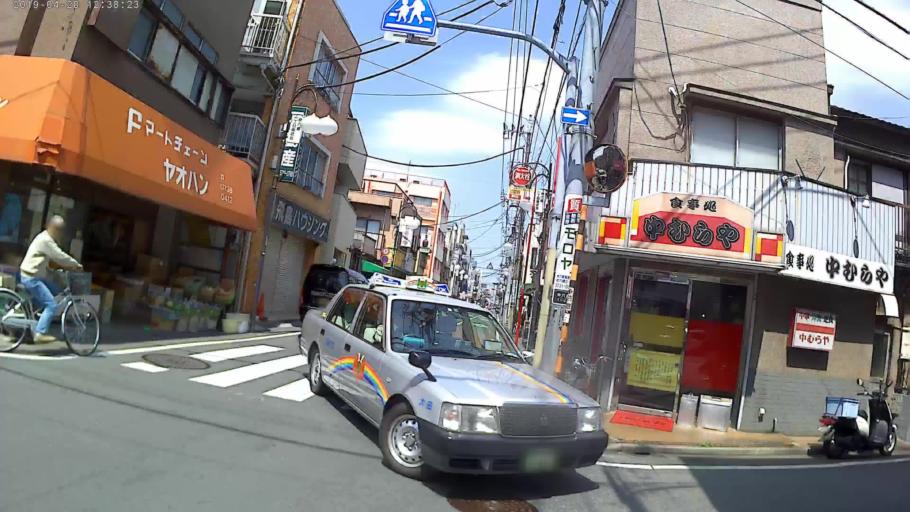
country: JP
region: Kanagawa
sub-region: Kawasaki-shi
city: Kawasaki
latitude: 35.5525
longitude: 139.7150
